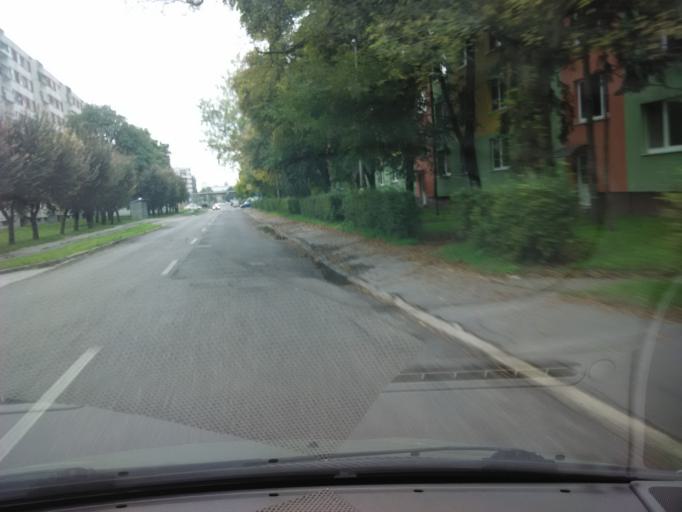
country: SK
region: Nitriansky
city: Levice
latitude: 48.2117
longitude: 18.6050
